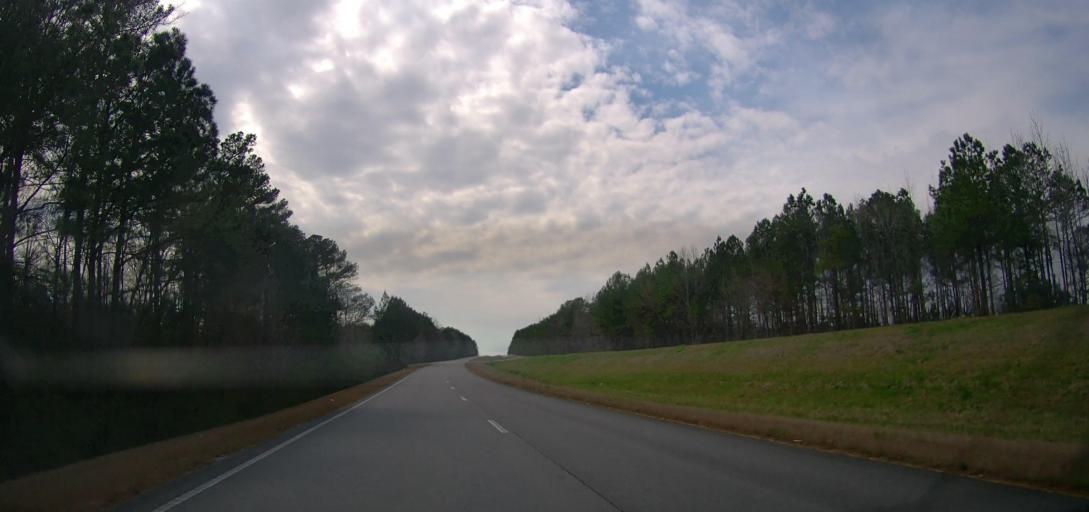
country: US
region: Alabama
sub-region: Marion County
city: Winfield
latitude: 33.9304
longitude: -87.6893
